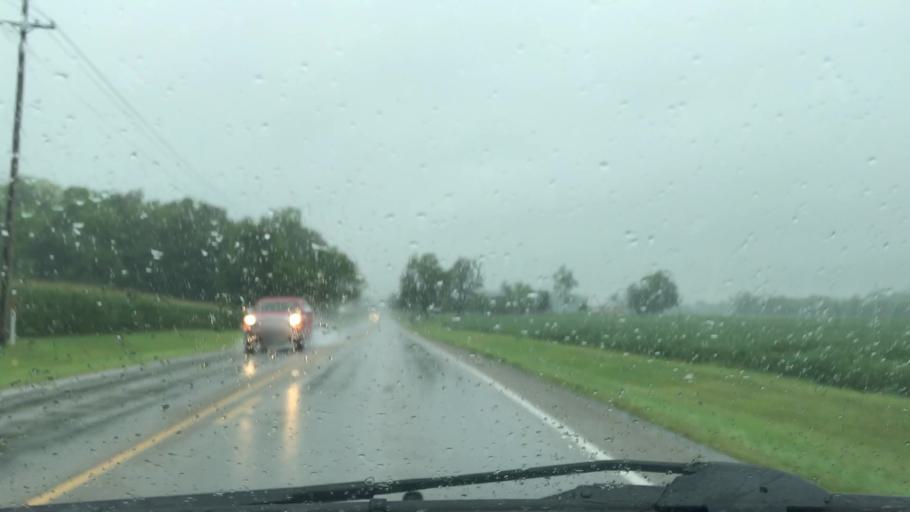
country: US
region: Indiana
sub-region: Hamilton County
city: Sheridan
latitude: 40.1168
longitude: -86.1794
